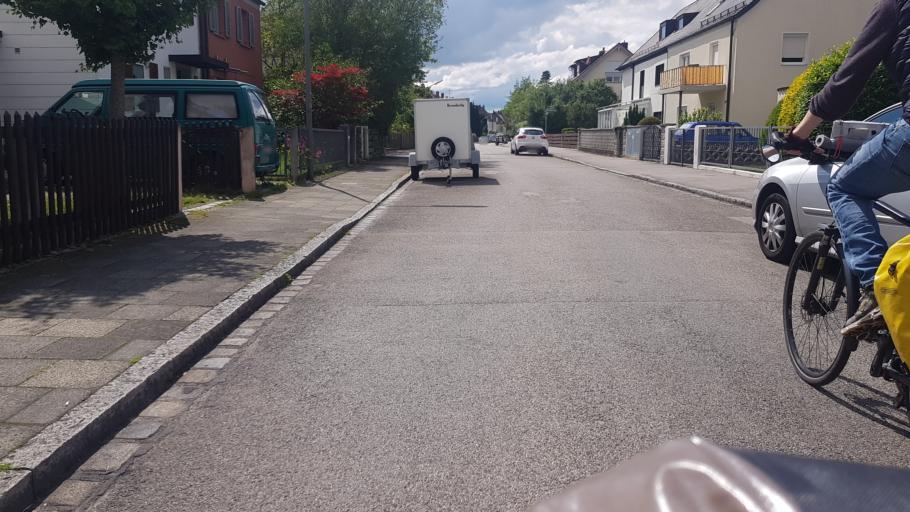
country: DE
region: Bavaria
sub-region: Upper Bavaria
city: Pasing
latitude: 48.1345
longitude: 11.4883
